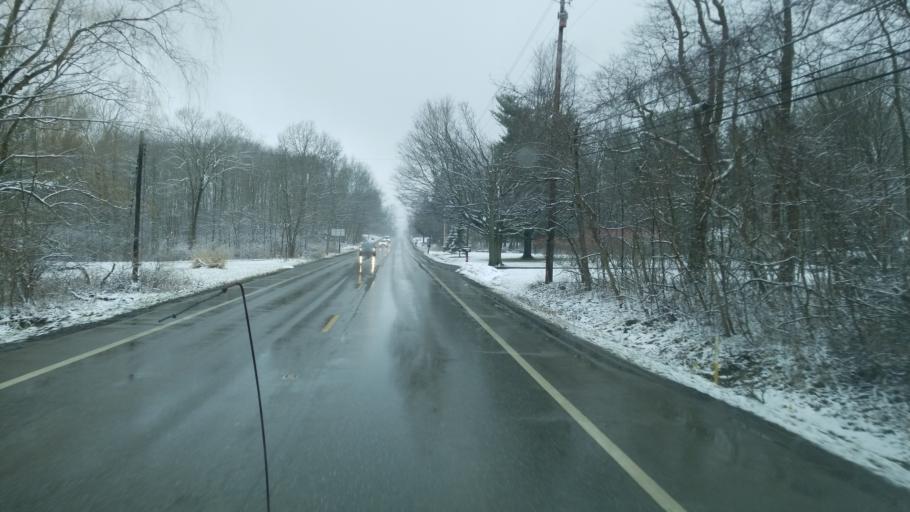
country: US
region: Ohio
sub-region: Portage County
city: Hiram
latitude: 41.3102
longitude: -81.1744
